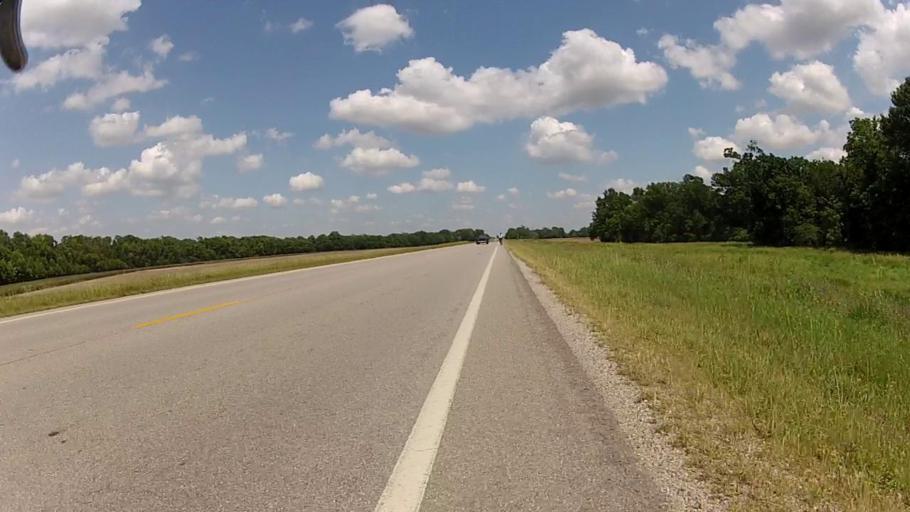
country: US
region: Kansas
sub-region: Labette County
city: Altamont
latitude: 37.1938
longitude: -95.2020
